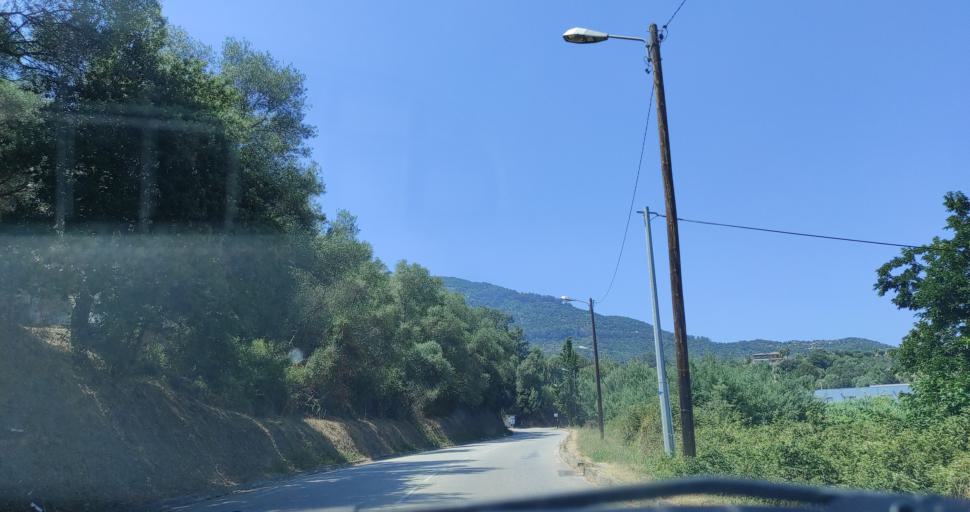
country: FR
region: Corsica
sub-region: Departement de la Corse-du-Sud
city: Ajaccio
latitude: 41.9405
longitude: 8.7373
